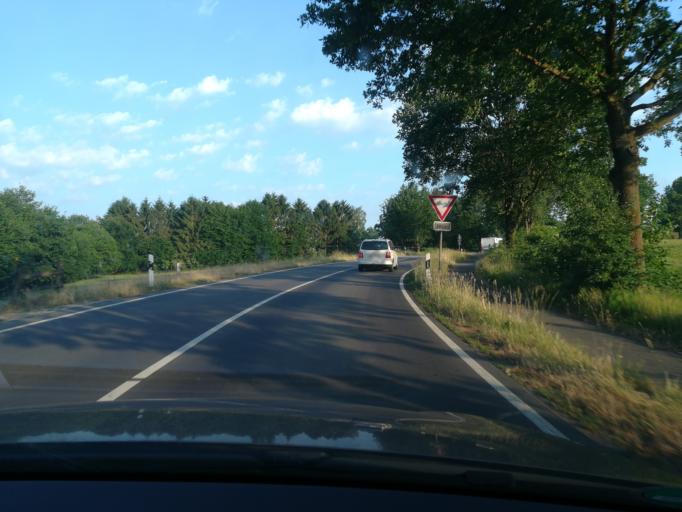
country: DE
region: Schleswig-Holstein
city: Siek
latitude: 53.6328
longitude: 10.3100
